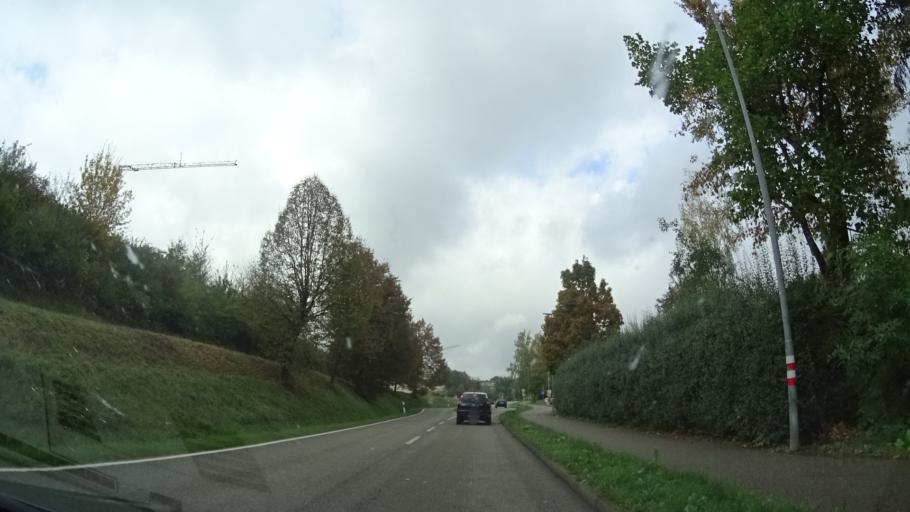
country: DE
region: Baden-Wuerttemberg
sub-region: Karlsruhe Region
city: Konigsbach-Stein
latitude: 48.9631
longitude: 8.6341
